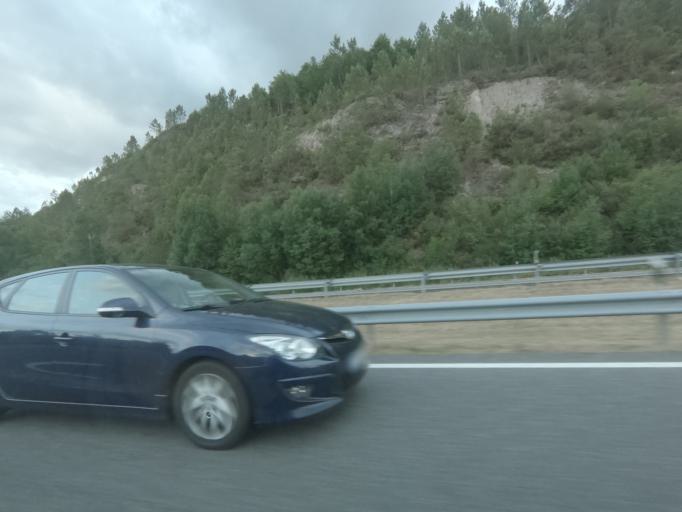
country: ES
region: Galicia
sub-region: Provincia de Ourense
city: Carballeda de Avia
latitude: 42.3087
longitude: -8.1750
